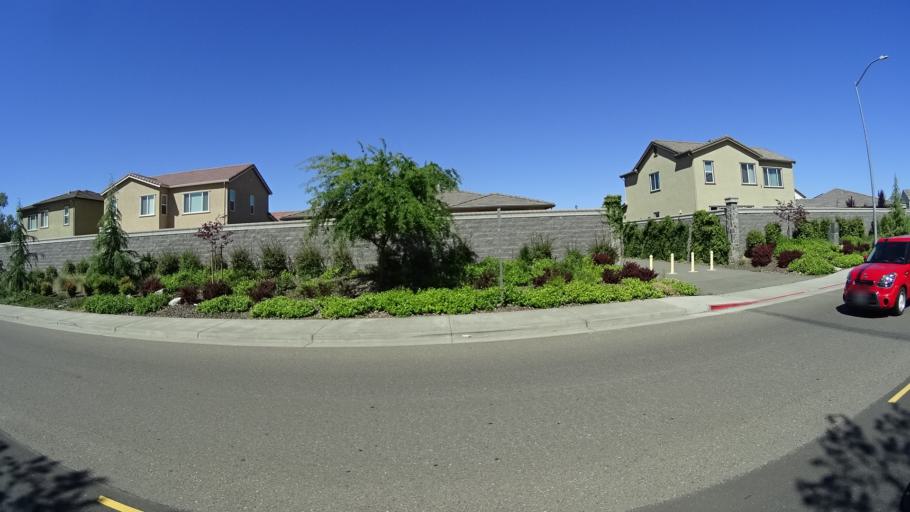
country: US
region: California
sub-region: Placer County
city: Rocklin
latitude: 38.8055
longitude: -121.2193
